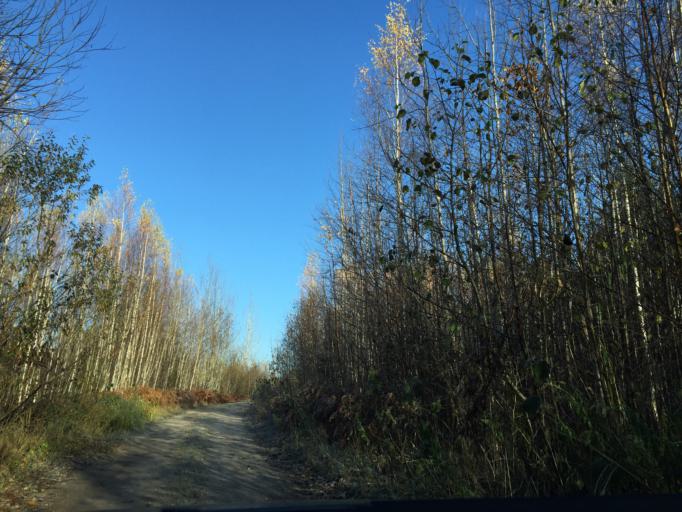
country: LV
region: Aizkraukles Rajons
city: Aizkraukle
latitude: 56.7138
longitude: 25.2993
